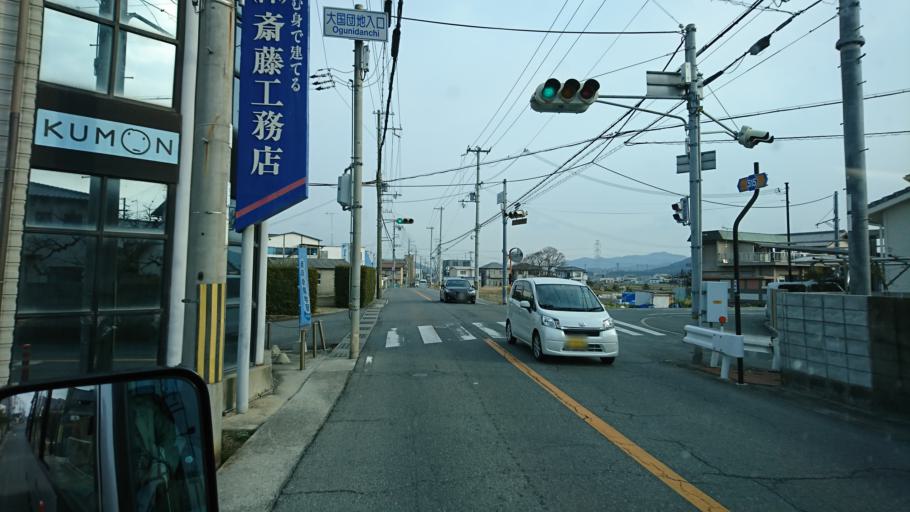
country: JP
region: Hyogo
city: Kakogawacho-honmachi
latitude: 34.7947
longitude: 134.8131
